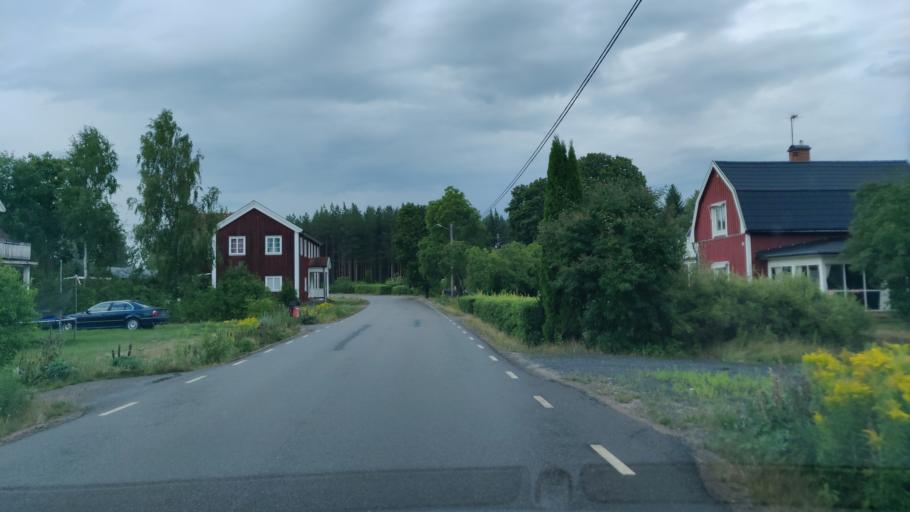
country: SE
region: Vaermland
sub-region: Munkfors Kommun
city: Munkfors
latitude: 59.8659
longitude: 13.5445
